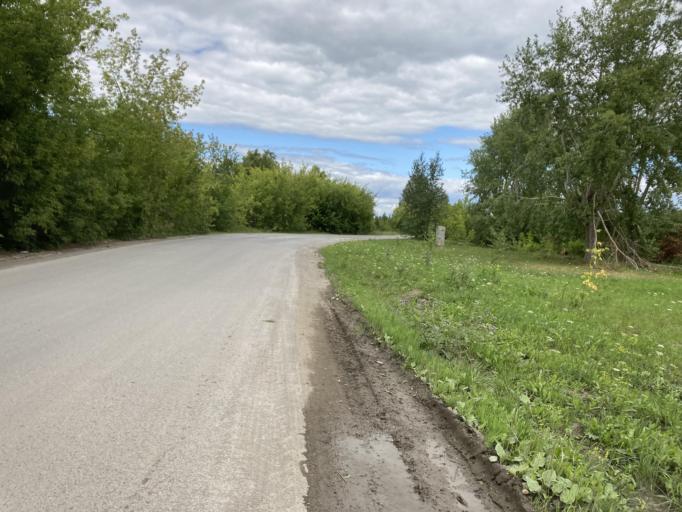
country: RU
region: Sverdlovsk
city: Bogdanovich
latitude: 56.7860
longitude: 62.0660
